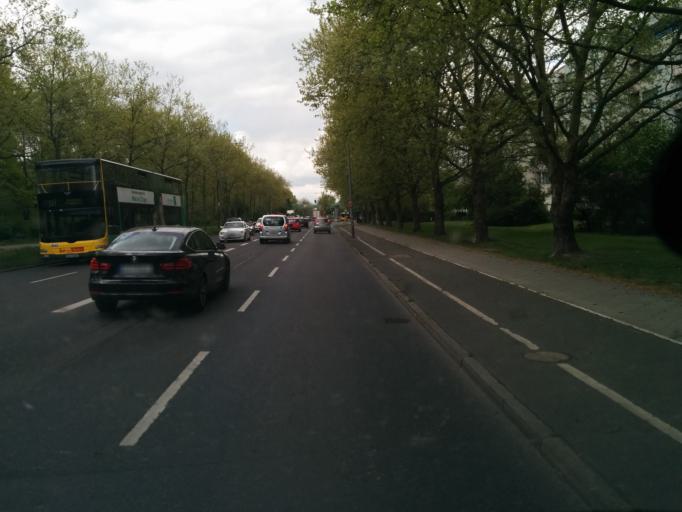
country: DE
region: Berlin
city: Staaken
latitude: 52.5212
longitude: 13.1578
